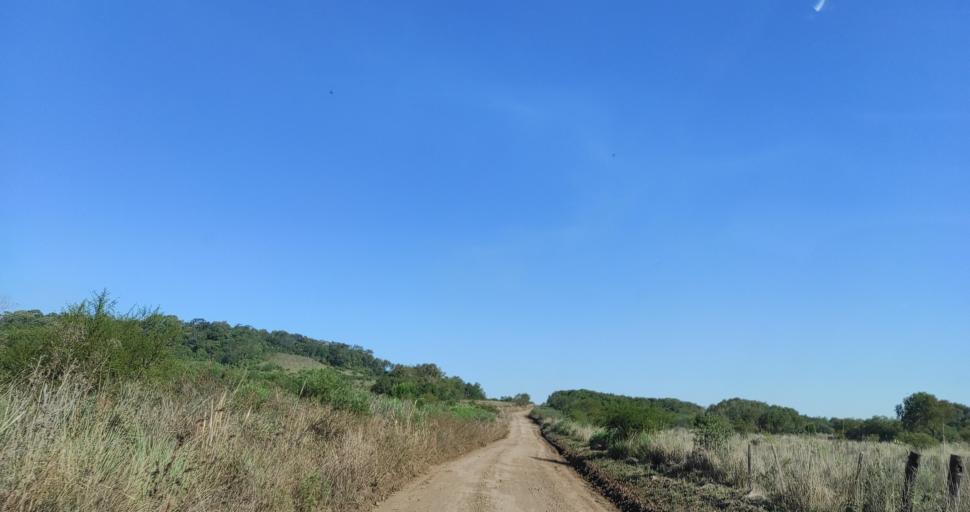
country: AR
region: Misiones
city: Cerro Cora
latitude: -27.6653
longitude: -55.6598
